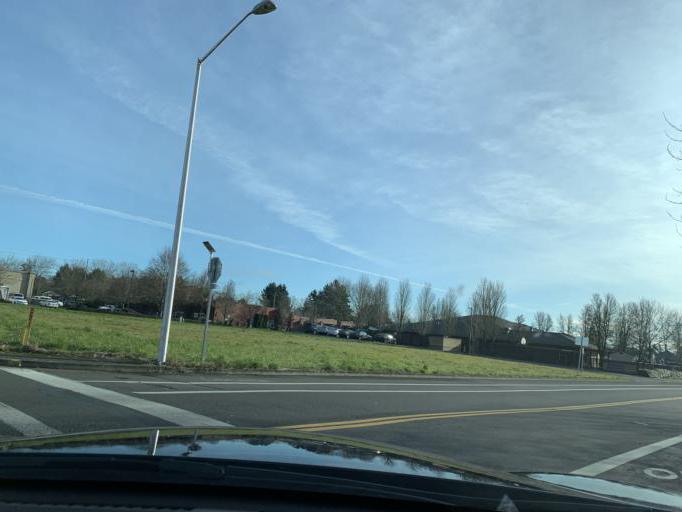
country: US
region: Washington
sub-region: Clark County
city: Mill Plain
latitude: 45.6001
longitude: -122.5060
